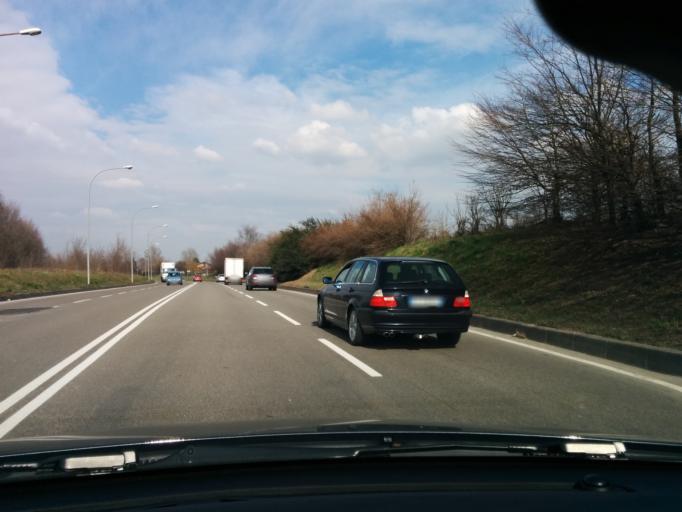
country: IT
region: Emilia-Romagna
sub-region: Provincia di Bologna
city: Progresso
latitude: 44.5457
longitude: 11.3466
